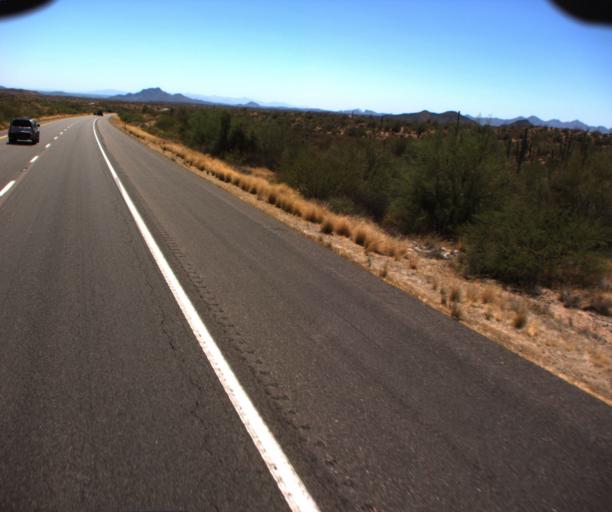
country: US
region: Arizona
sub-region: Maricopa County
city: Rio Verde
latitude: 33.6489
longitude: -111.5305
